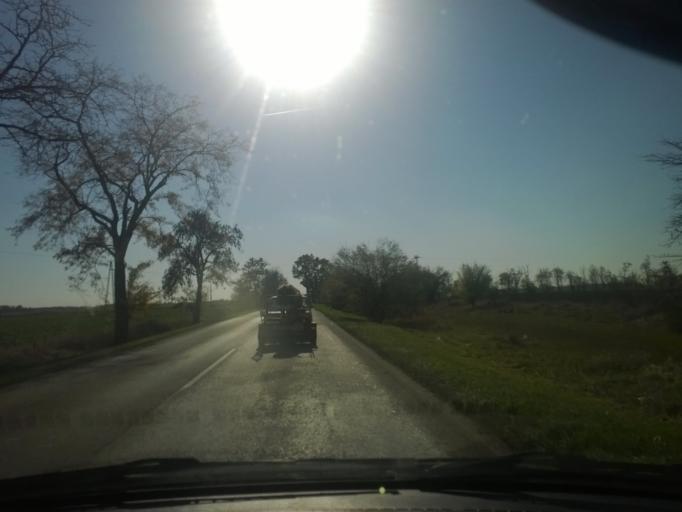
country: HU
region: Csongrad
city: Szegvar
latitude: 46.5486
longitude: 20.3169
